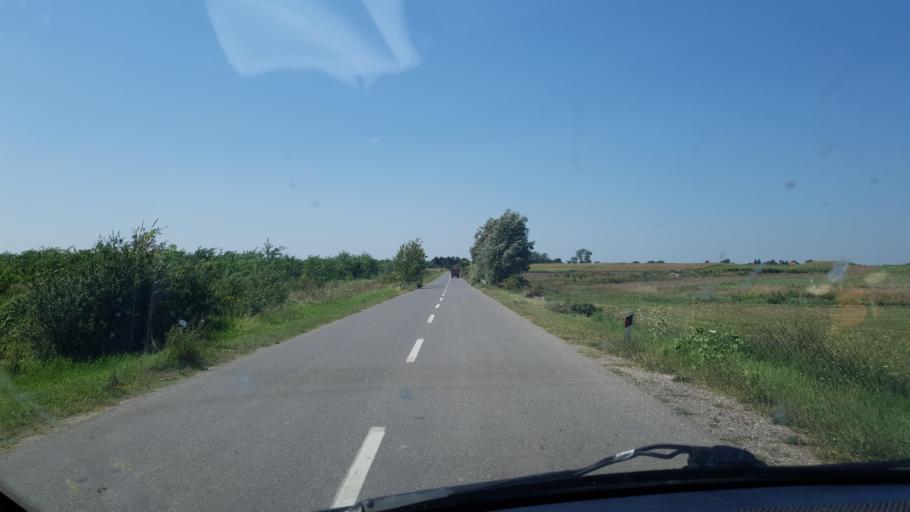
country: RS
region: Autonomna Pokrajina Vojvodina
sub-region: Juznobacki Okrug
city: Kovilj
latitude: 45.2213
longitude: 20.0480
